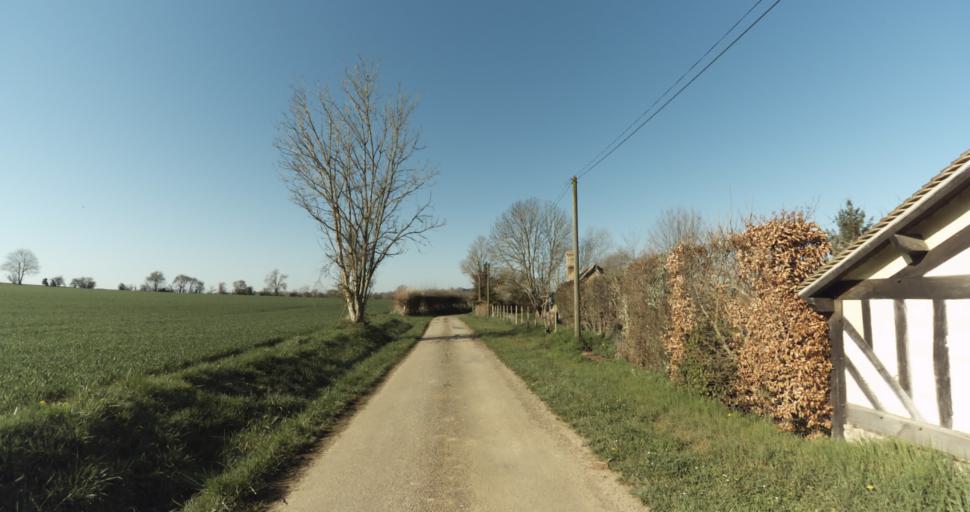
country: FR
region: Lower Normandy
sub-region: Departement du Calvados
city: Saint-Pierre-sur-Dives
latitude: 48.9646
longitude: 0.0251
